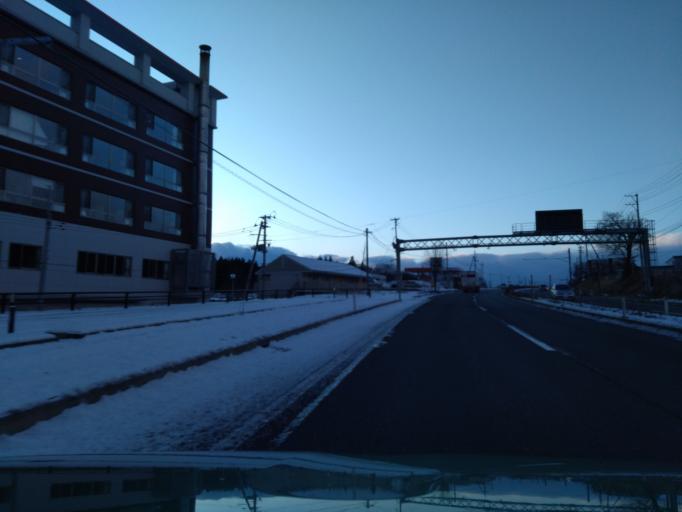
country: JP
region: Iwate
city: Shizukuishi
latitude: 39.6992
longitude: 141.0571
